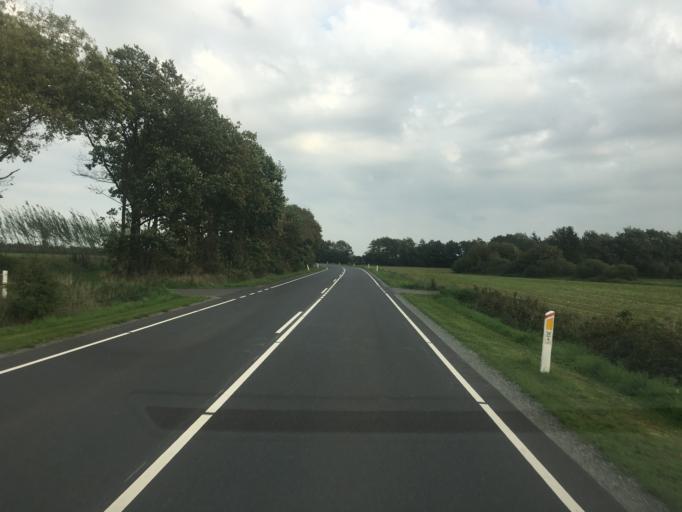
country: DK
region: South Denmark
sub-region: Tonder Kommune
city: Logumkloster
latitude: 54.9763
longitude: 9.0427
